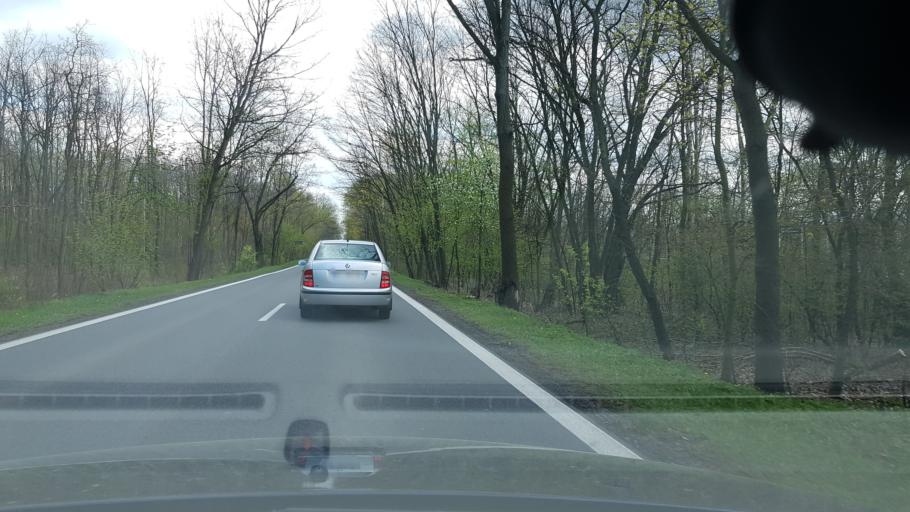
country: PL
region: Masovian Voivodeship
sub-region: Powiat minski
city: Sulejowek
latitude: 52.2533
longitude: 21.2470
